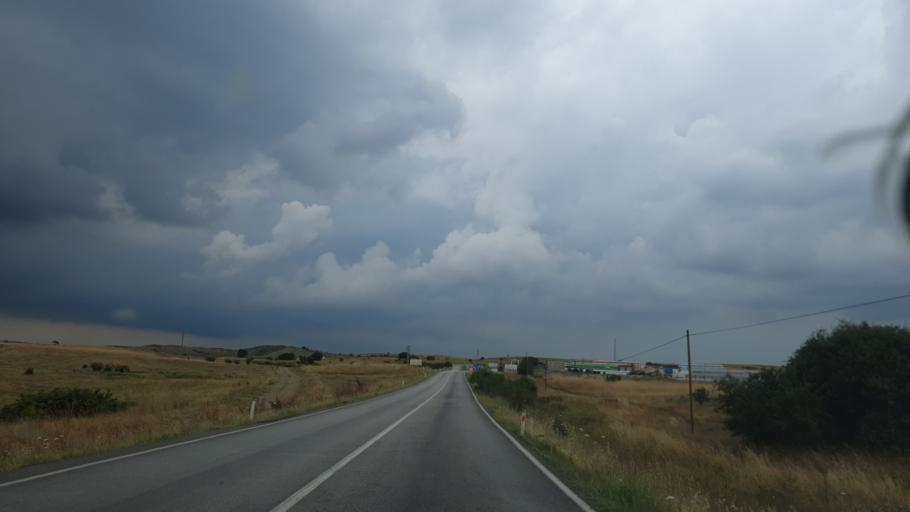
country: TR
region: Tekirdag
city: Hayrabolu
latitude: 41.2196
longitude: 27.0527
